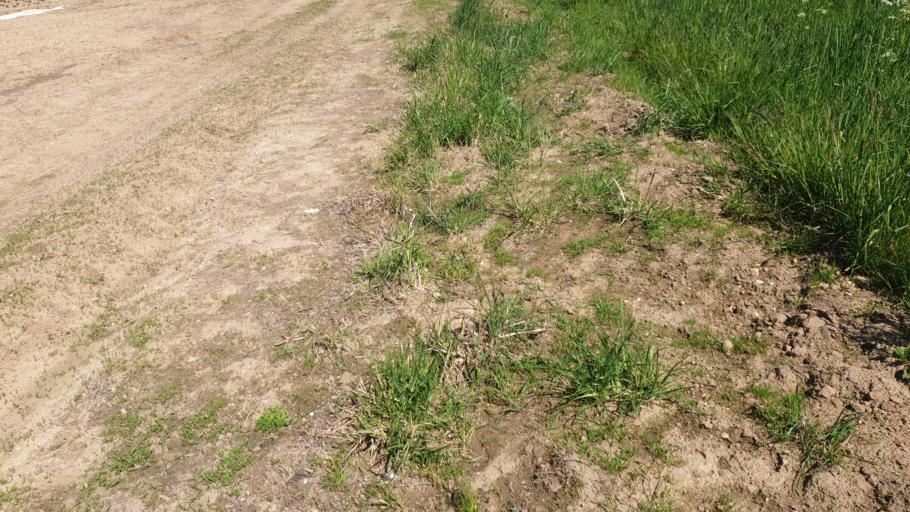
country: GB
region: England
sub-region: Essex
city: Great Bentley
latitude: 51.8600
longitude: 1.0453
